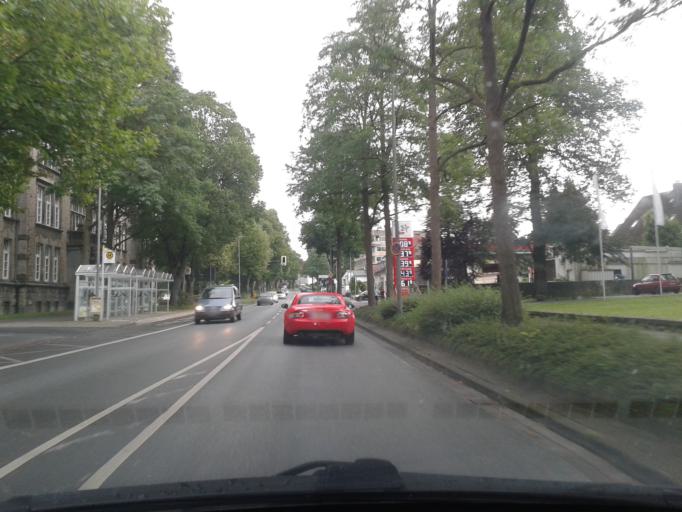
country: DE
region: North Rhine-Westphalia
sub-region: Regierungsbezirk Detmold
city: Detmold
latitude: 51.9309
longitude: 8.8820
